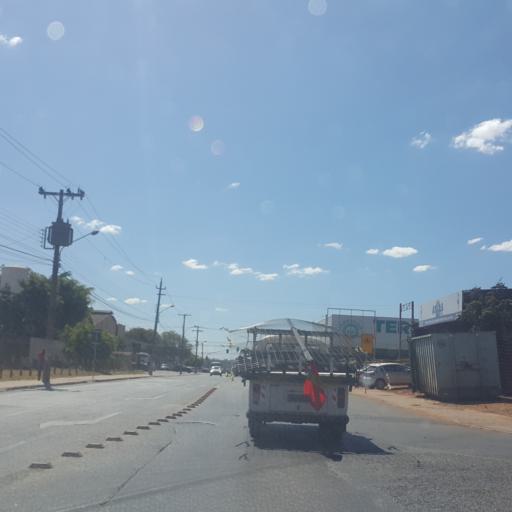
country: BR
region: Federal District
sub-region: Brasilia
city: Brasilia
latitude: -15.8069
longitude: -48.0743
